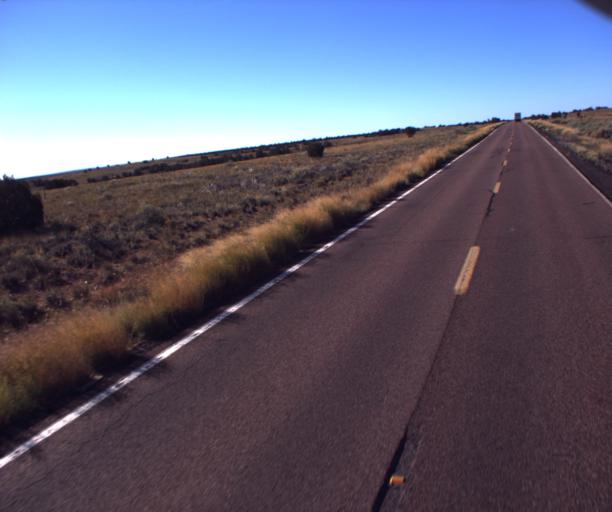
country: US
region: Arizona
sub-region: Navajo County
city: Heber-Overgaard
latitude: 34.5485
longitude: -110.4168
